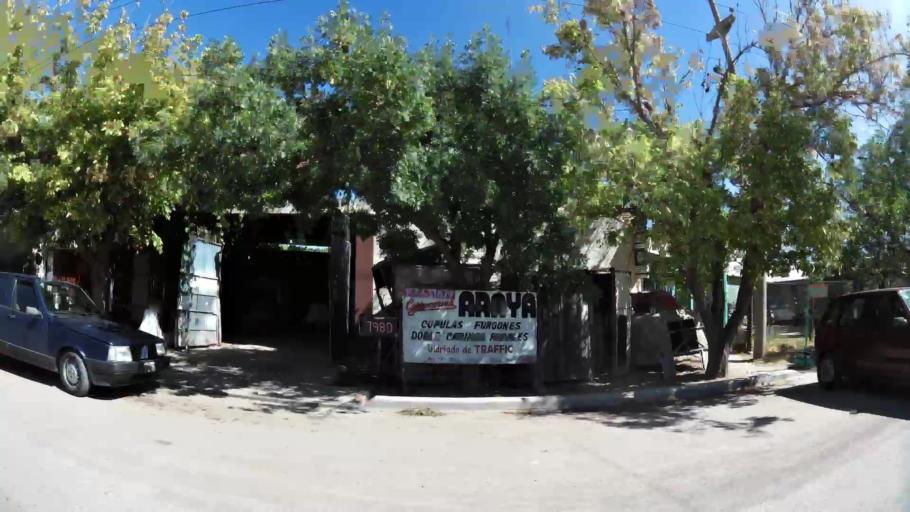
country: AR
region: Mendoza
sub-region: Departamento de Godoy Cruz
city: Godoy Cruz
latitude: -32.9655
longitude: -68.8412
